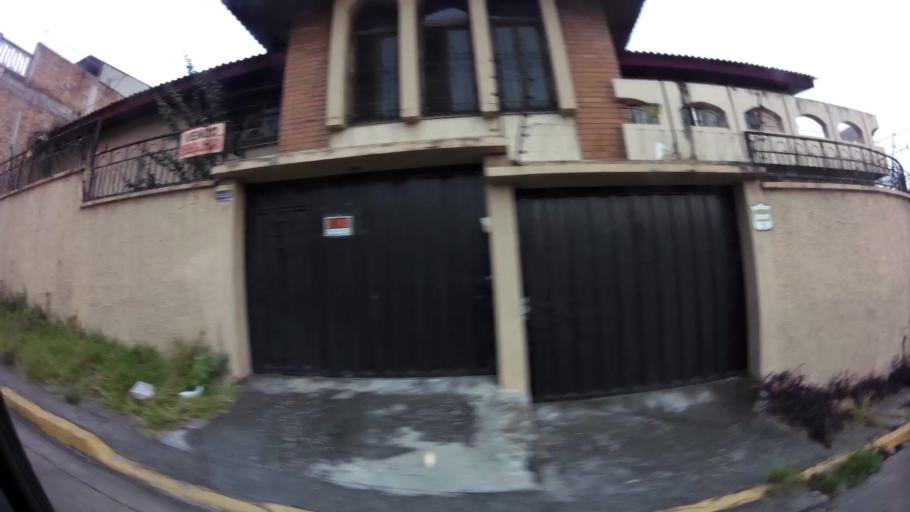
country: HN
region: Francisco Morazan
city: Tegucigalpa
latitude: 14.0936
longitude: -87.1958
